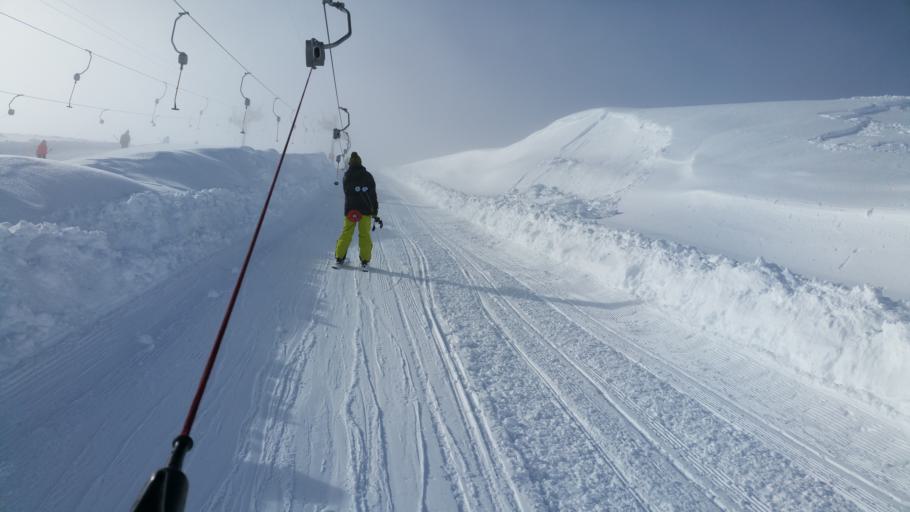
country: FR
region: Rhone-Alpes
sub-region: Departement de la Savoie
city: Saint-Etienne-de-Cuines
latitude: 45.2440
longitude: 6.2175
